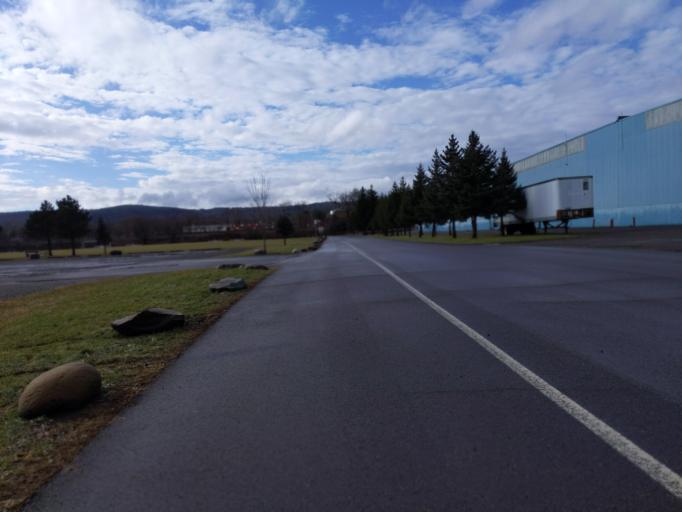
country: US
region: New York
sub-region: Chemung County
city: Elmira Heights
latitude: 42.1178
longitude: -76.8181
